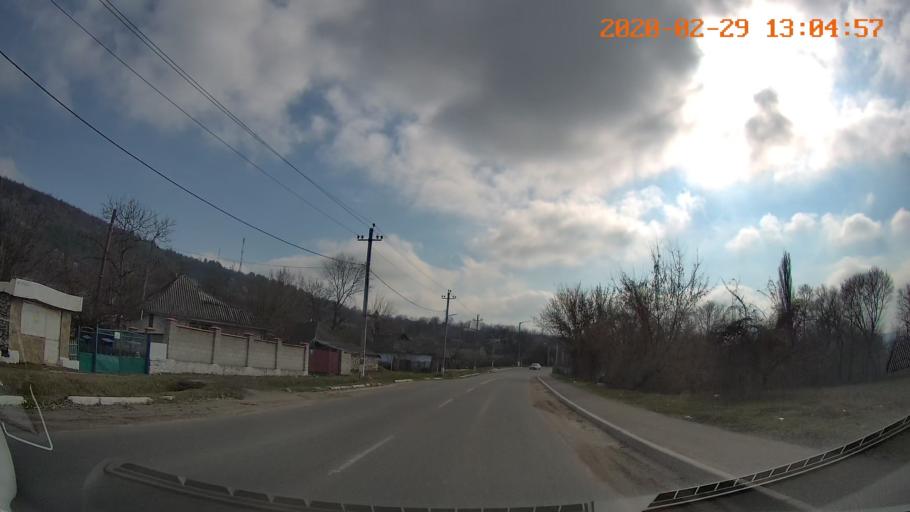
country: MD
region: Telenesti
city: Camenca
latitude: 48.0240
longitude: 28.7079
